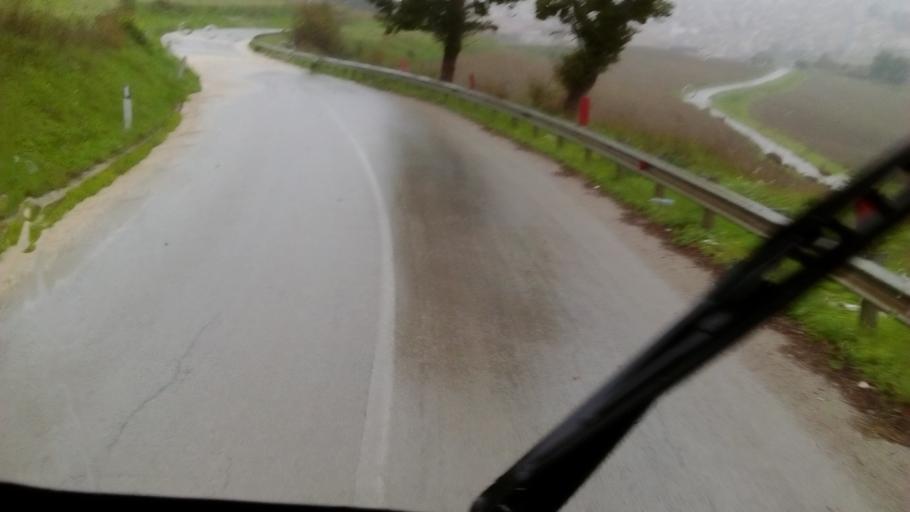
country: IT
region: Sicily
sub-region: Enna
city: Pietraperzia
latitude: 37.4190
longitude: 14.1507
